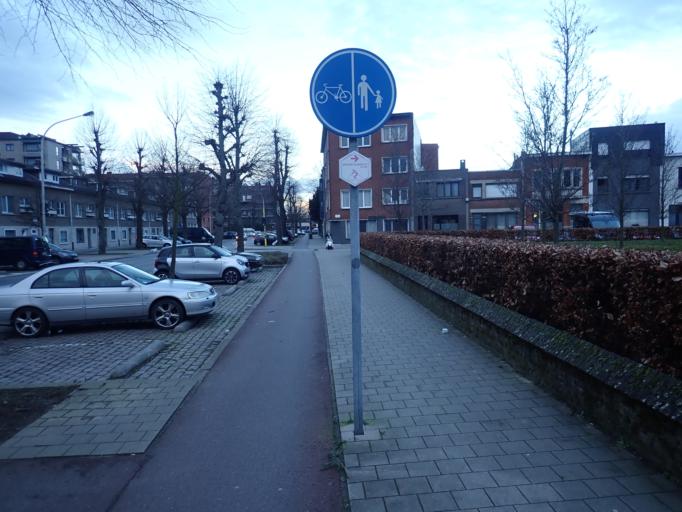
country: BE
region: Flanders
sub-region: Provincie Antwerpen
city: Mortsel
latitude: 51.2042
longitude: 4.4478
